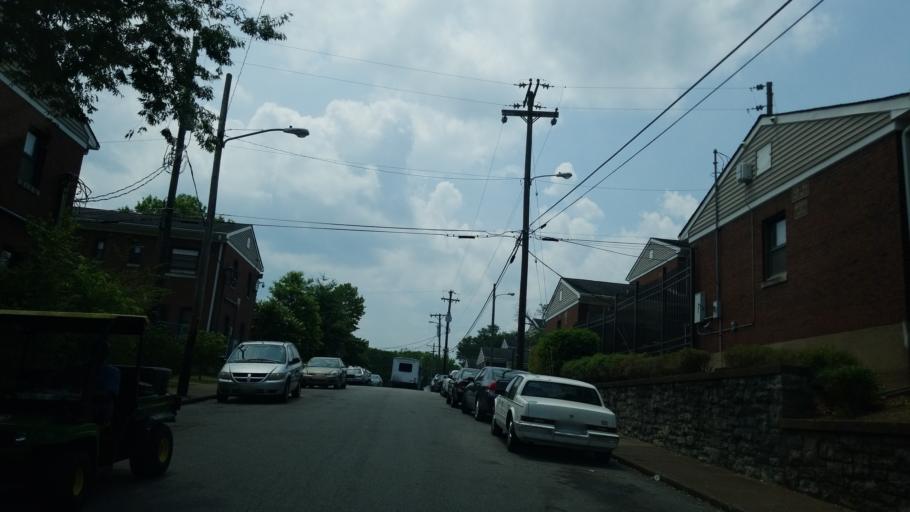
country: US
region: Tennessee
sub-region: Davidson County
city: Nashville
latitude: 36.1672
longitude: -86.7990
